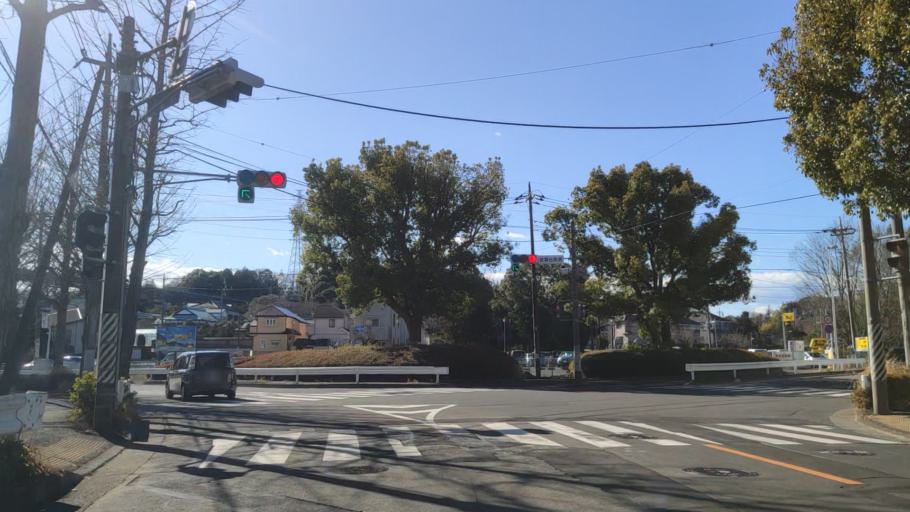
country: JP
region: Kanagawa
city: Minami-rinkan
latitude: 35.5012
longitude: 139.5004
